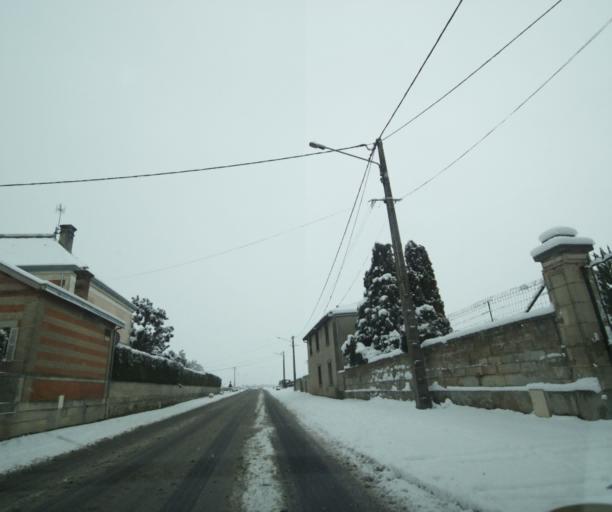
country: FR
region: Champagne-Ardenne
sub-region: Departement de la Haute-Marne
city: Saint-Dizier
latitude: 48.5820
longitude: 4.9040
